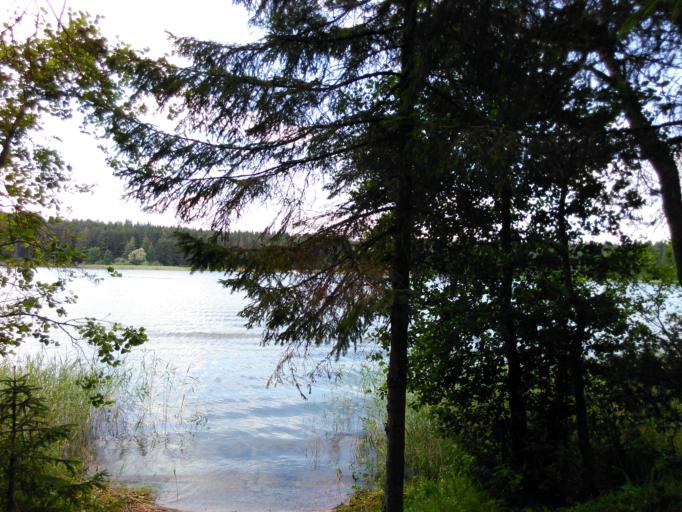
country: RU
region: Tverskaya
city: Ostashkov
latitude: 57.2437
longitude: 33.0138
